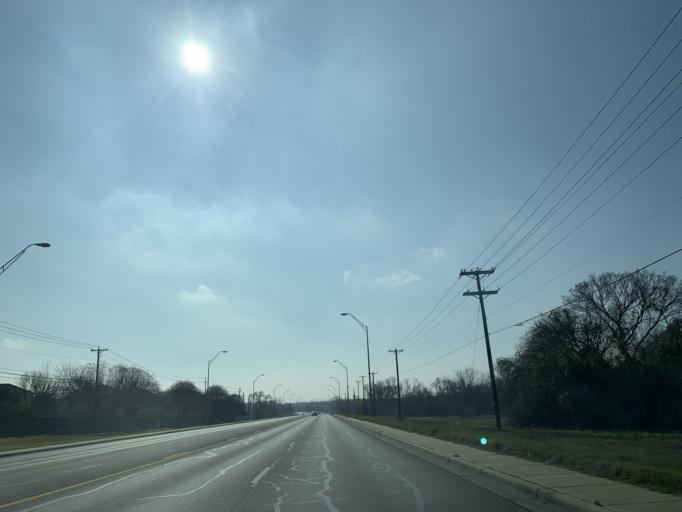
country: US
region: Texas
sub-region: Williamson County
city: Round Rock
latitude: 30.5382
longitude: -97.6515
